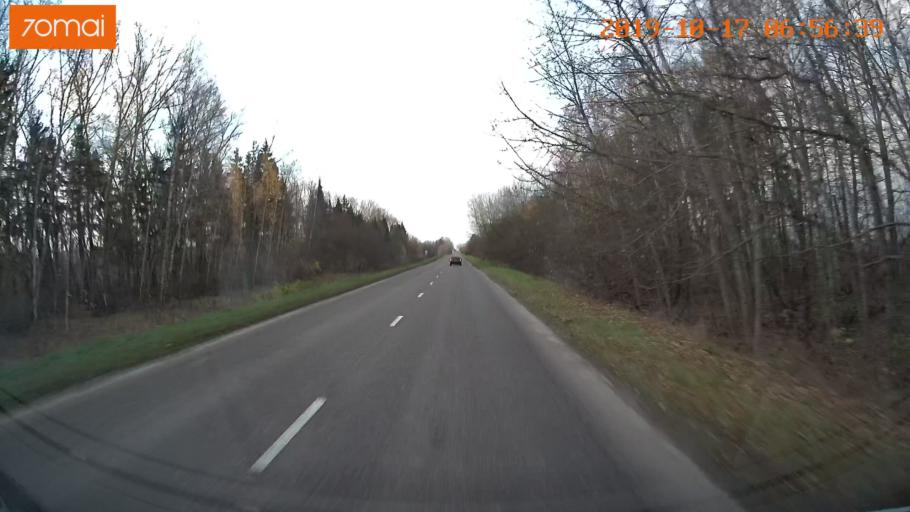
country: RU
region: Vladimir
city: Suzdal'
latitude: 56.4442
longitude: 40.4458
